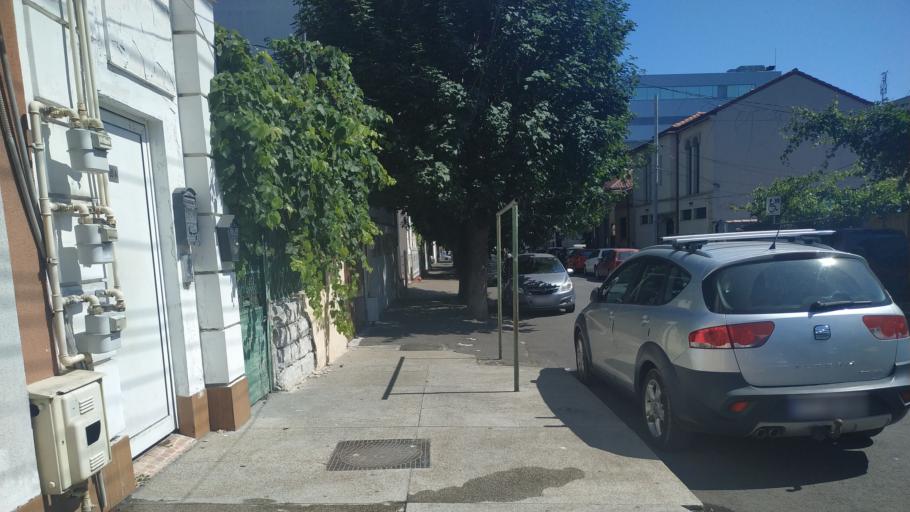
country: RO
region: Constanta
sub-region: Municipiul Constanta
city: Constanta
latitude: 44.1801
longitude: 28.6458
